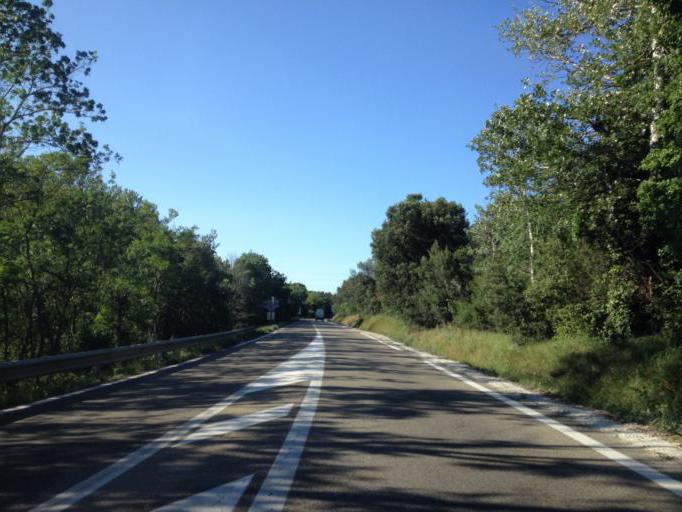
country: FR
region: Languedoc-Roussillon
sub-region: Departement du Gard
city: Montfaucon
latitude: 44.0812
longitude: 4.7775
